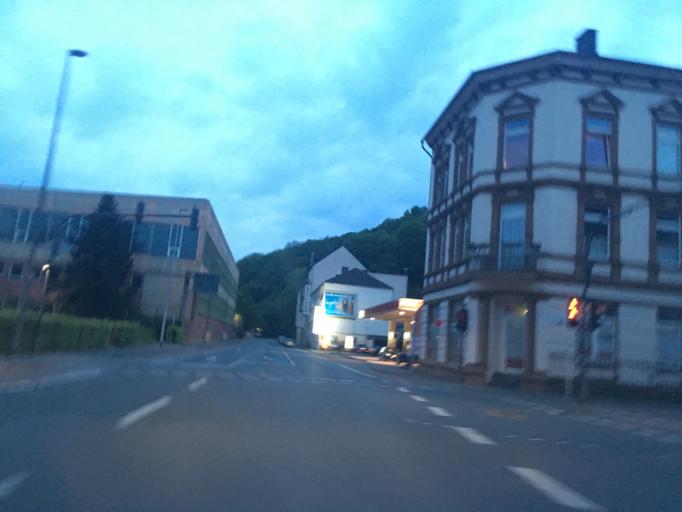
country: DE
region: North Rhine-Westphalia
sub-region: Regierungsbezirk Dusseldorf
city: Wuppertal
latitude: 51.2460
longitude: 7.1058
